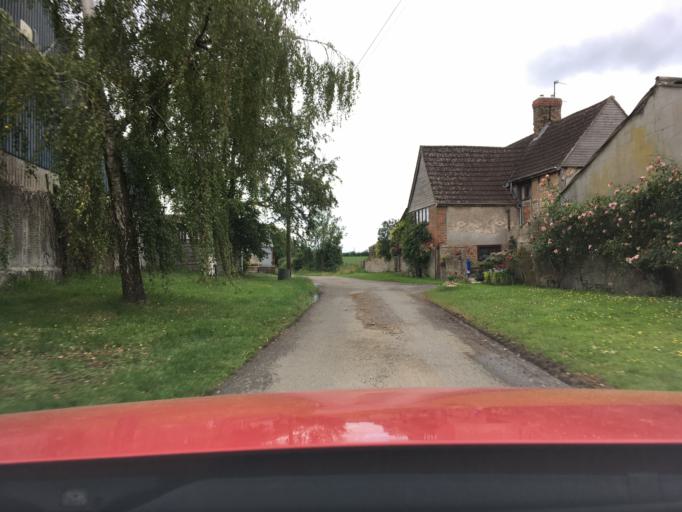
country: GB
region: England
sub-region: Gloucestershire
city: Cinderford
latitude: 51.7949
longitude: -2.4074
